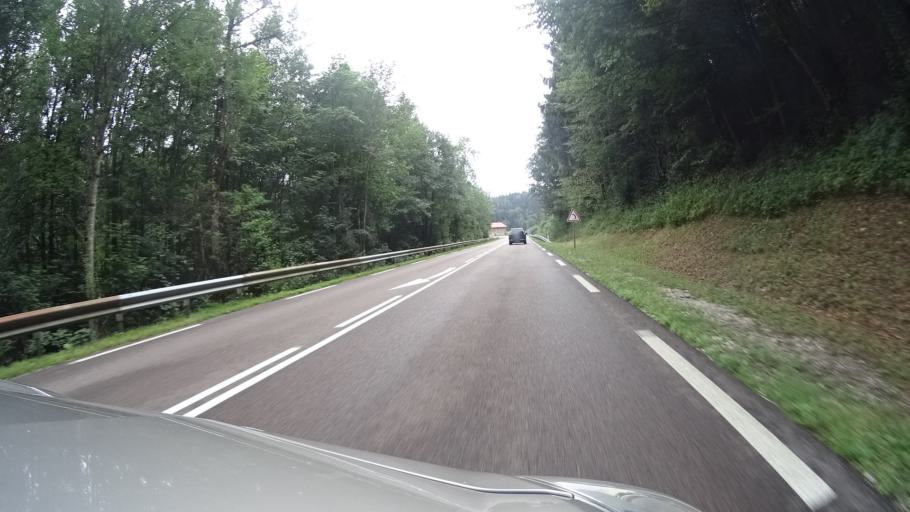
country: FR
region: Franche-Comte
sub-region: Departement du Jura
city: Champagnole
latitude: 46.6445
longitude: 5.9403
